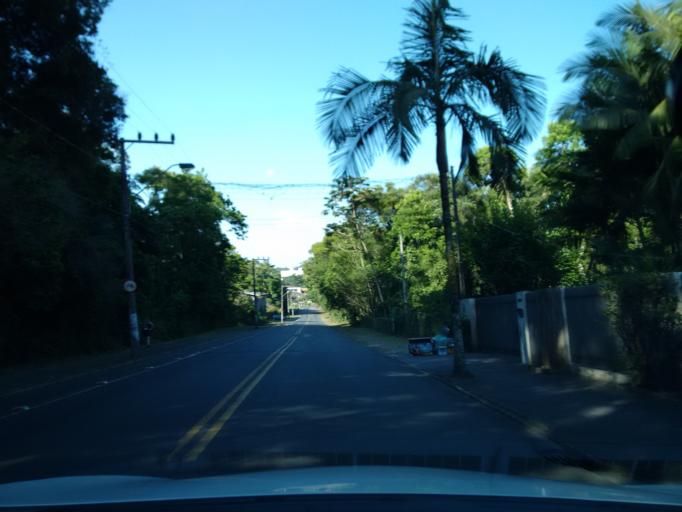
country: BR
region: Santa Catarina
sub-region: Blumenau
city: Blumenau
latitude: -26.9050
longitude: -49.0696
